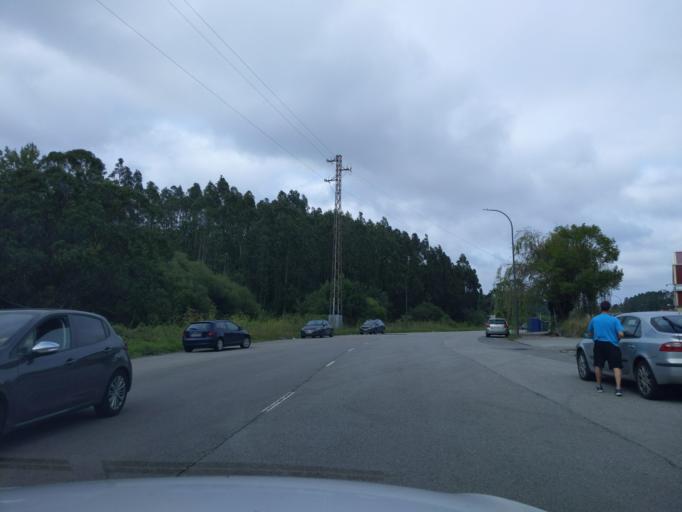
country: ES
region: Asturias
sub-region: Province of Asturias
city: Aviles
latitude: 43.6019
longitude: -5.9059
